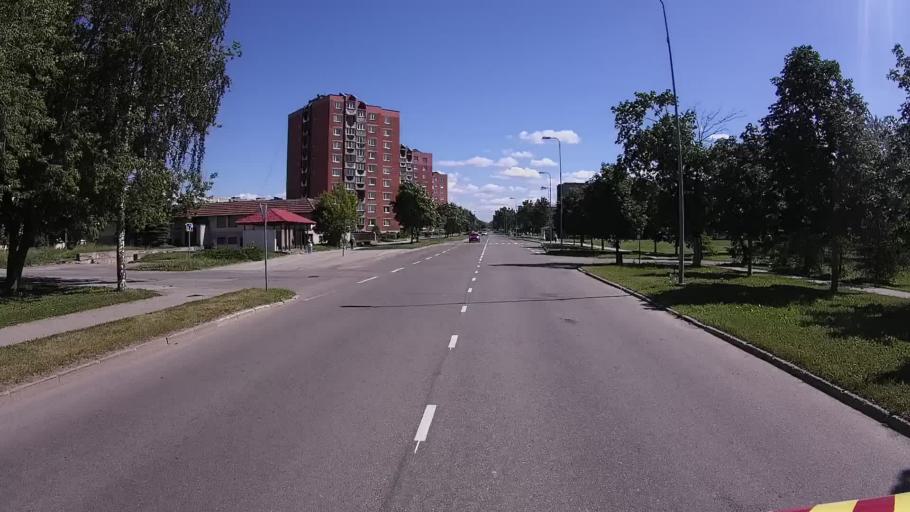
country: EE
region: Ida-Virumaa
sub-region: Kohtla-Jaerve linn
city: Kohtla-Jarve
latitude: 59.4086
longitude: 27.2802
